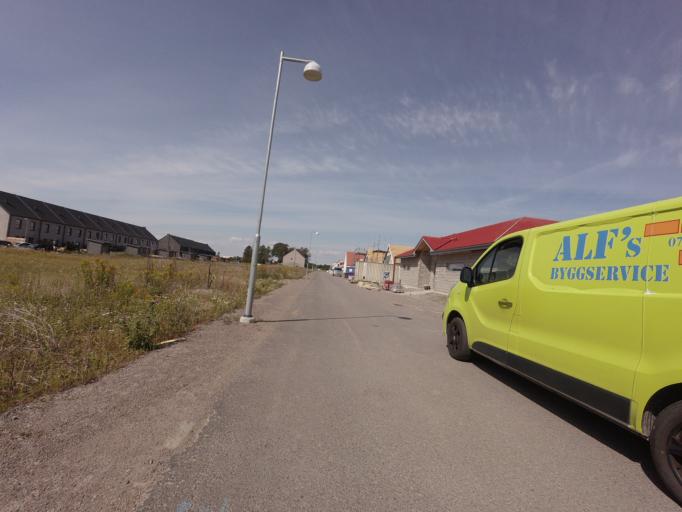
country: SE
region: Skane
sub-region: Landskrona
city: Landskrona
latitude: 55.9015
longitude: 12.8220
